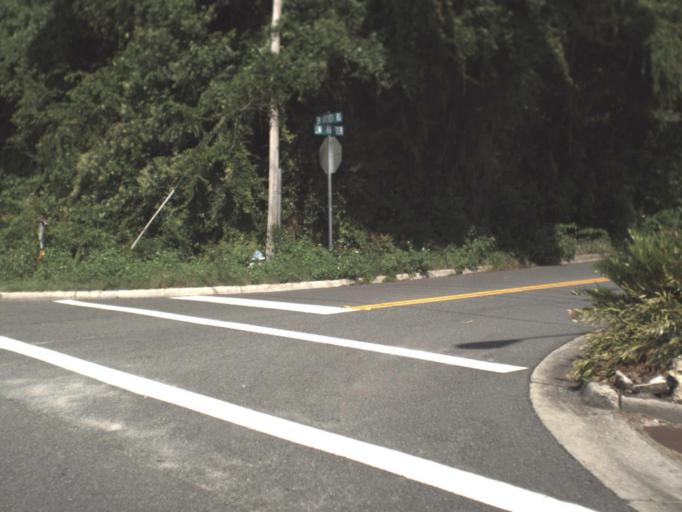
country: US
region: Florida
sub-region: Alachua County
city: Gainesville
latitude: 29.6019
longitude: -82.4157
